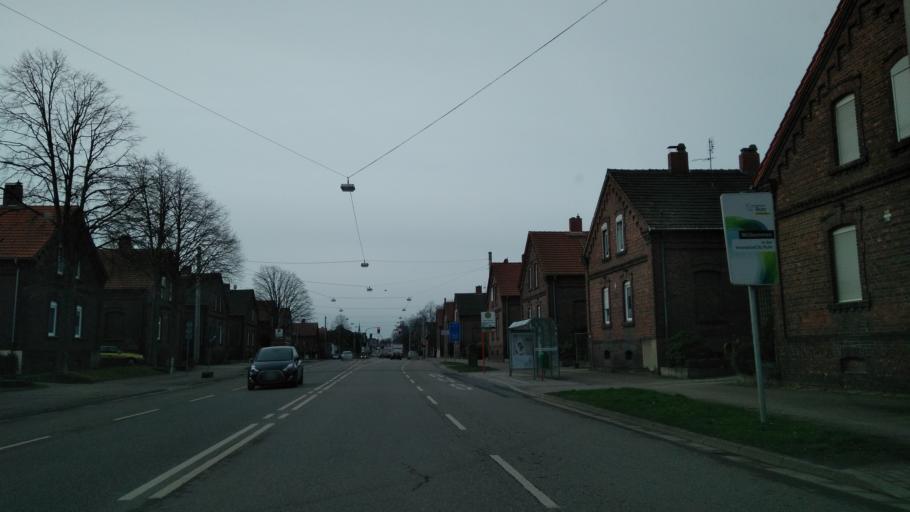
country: DE
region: North Rhine-Westphalia
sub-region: Regierungsbezirk Munster
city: Bottrop
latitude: 51.5546
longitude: 6.9438
